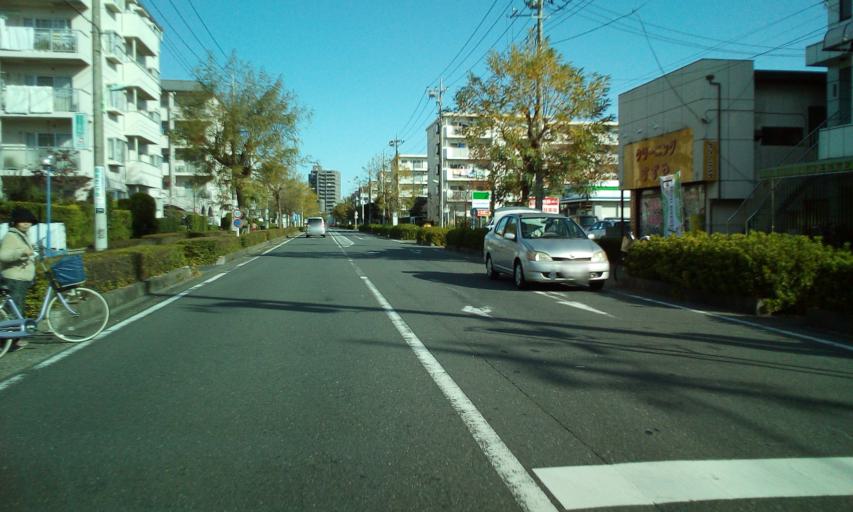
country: JP
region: Chiba
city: Nagareyama
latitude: 35.8550
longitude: 139.8869
